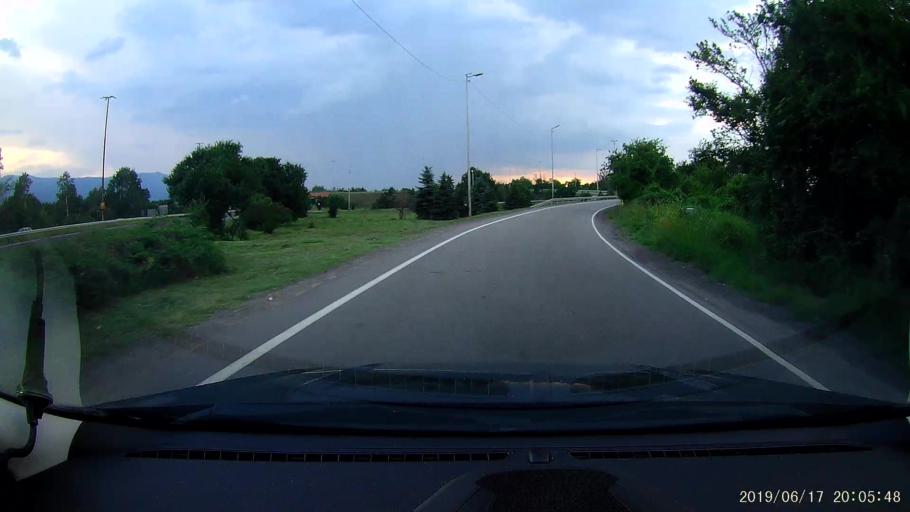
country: BG
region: Sofia-Capital
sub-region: Stolichna Obshtina
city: Sofia
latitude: 42.6331
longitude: 23.4513
